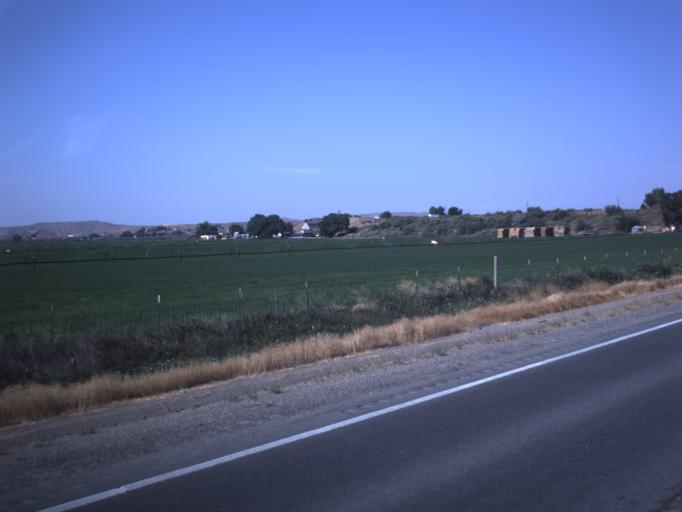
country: US
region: Utah
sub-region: Uintah County
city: Naples
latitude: 40.3695
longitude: -109.3697
